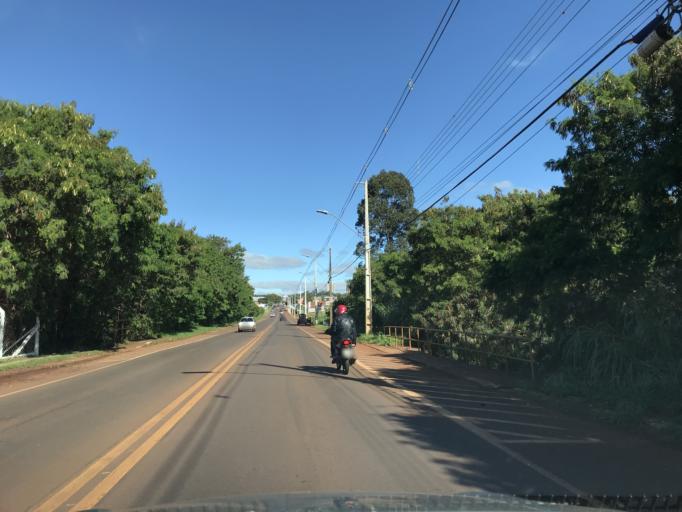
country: BR
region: Parana
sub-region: Cascavel
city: Cascavel
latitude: -24.9258
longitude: -53.4747
